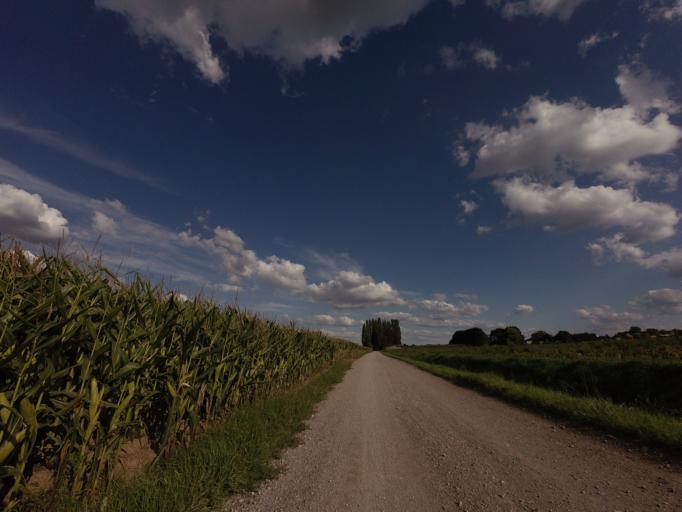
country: BE
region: Flanders
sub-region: Provincie Vlaams-Brabant
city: Meise
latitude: 50.9532
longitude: 4.3305
